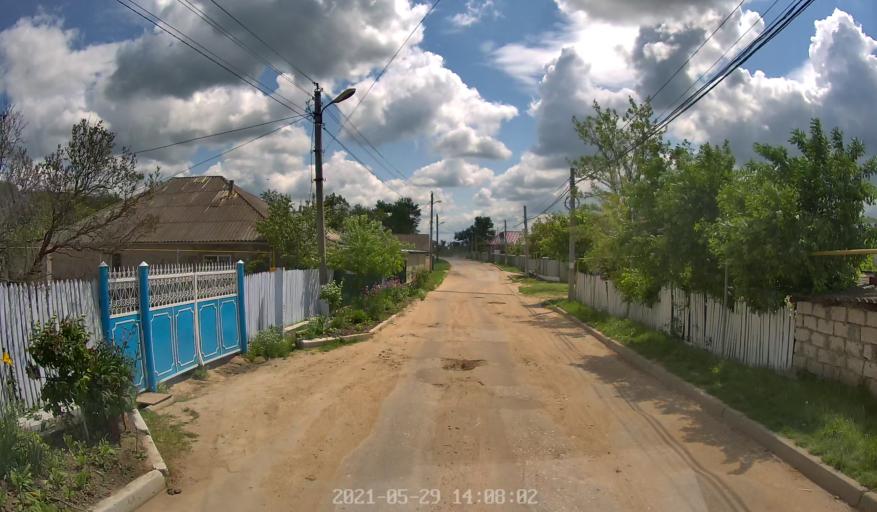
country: MD
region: Hincesti
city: Hincesti
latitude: 46.8286
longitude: 28.6766
